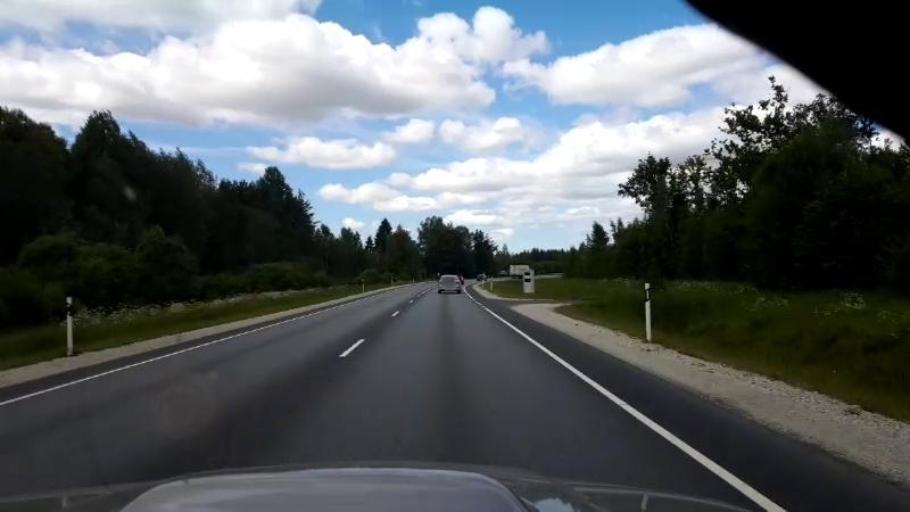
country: EE
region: Paernumaa
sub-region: Halinga vald
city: Parnu-Jaagupi
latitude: 58.6755
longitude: 24.4426
